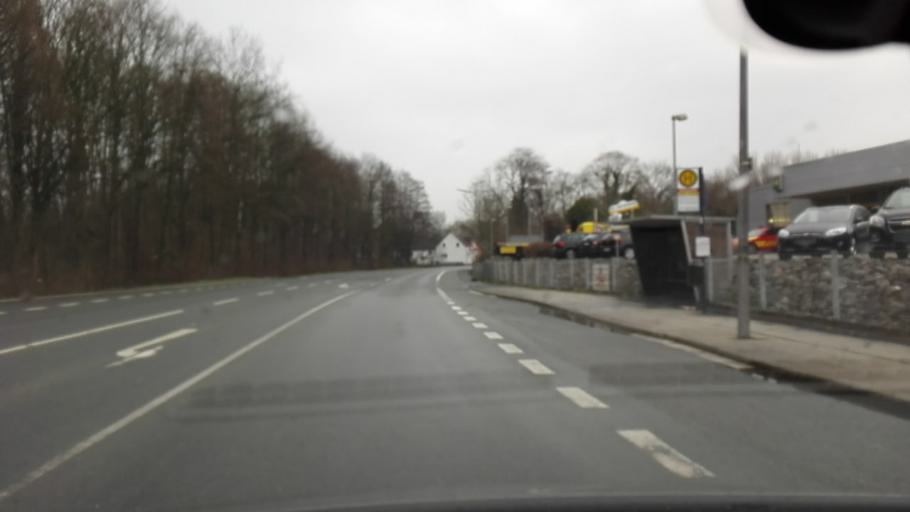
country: DE
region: North Rhine-Westphalia
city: Kamen
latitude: 51.5867
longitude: 7.6756
